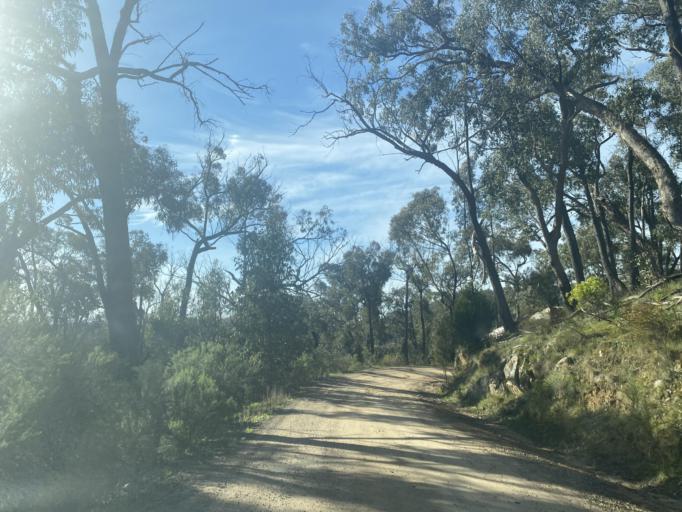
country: AU
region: Victoria
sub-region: Mansfield
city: Mansfield
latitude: -36.8373
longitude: 146.1665
